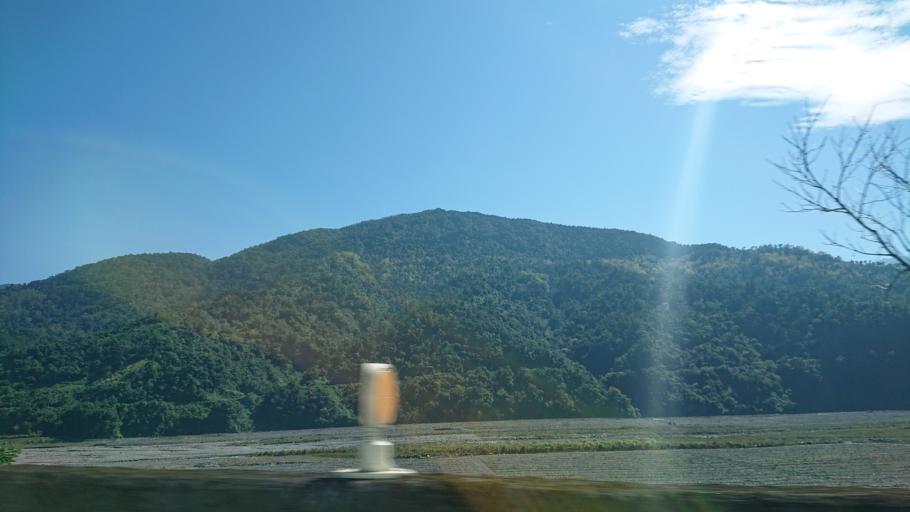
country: TW
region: Taiwan
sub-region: Yilan
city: Yilan
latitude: 24.5895
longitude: 121.5064
